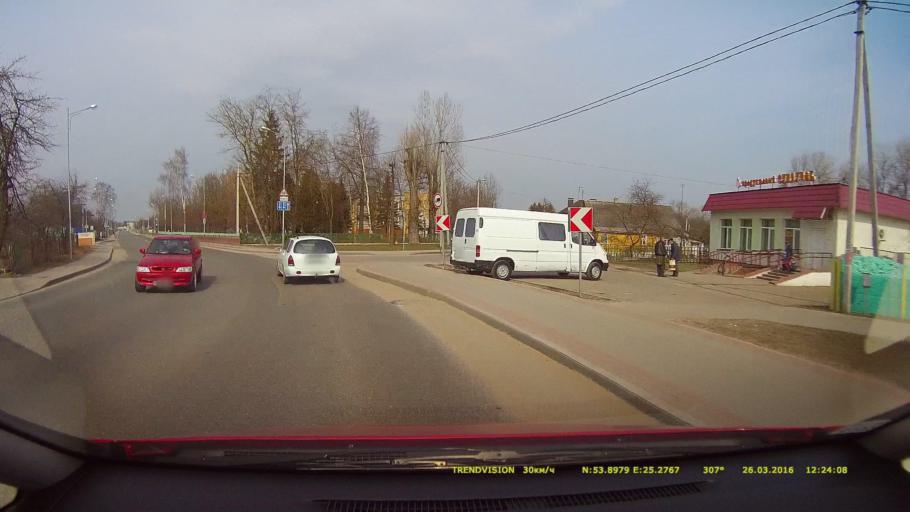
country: BY
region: Grodnenskaya
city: Lida
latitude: 53.8982
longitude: 25.2767
